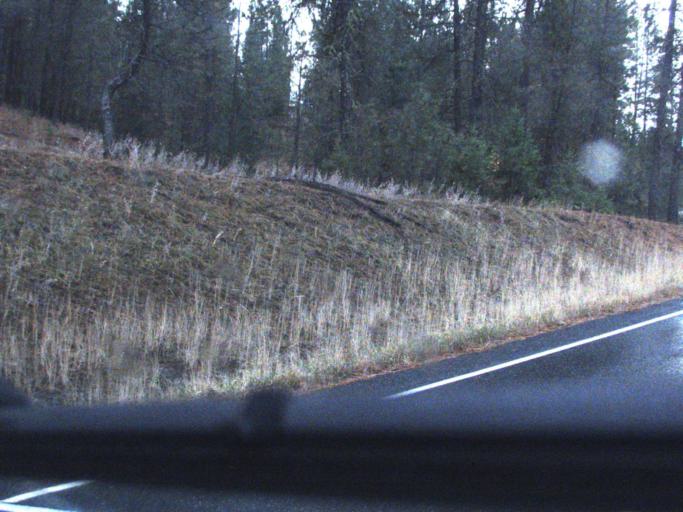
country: US
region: Washington
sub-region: Stevens County
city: Kettle Falls
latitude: 48.4848
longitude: -118.1714
